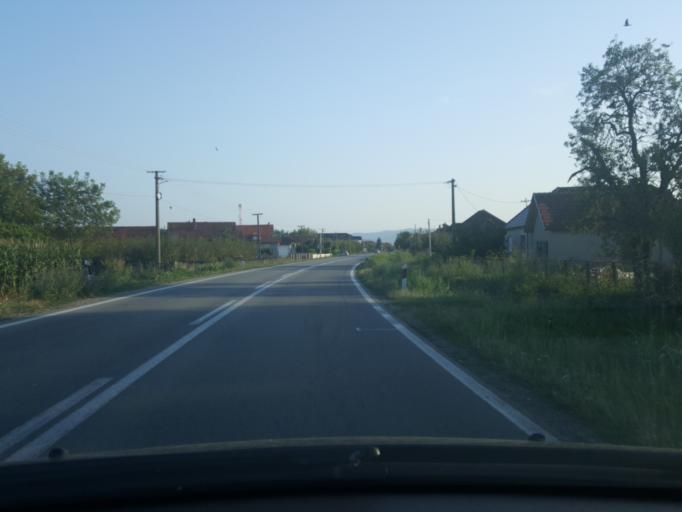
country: RS
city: Lipolist
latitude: 44.7455
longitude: 19.5265
